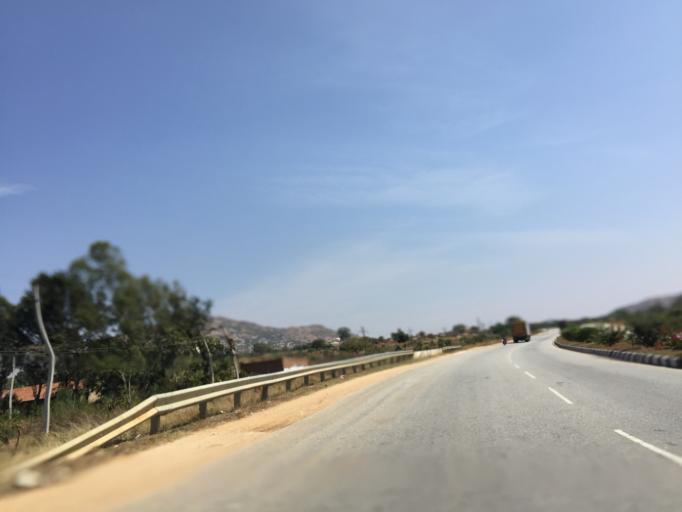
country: IN
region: Karnataka
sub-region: Kolar
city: Kolar
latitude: 13.1347
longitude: 78.0188
